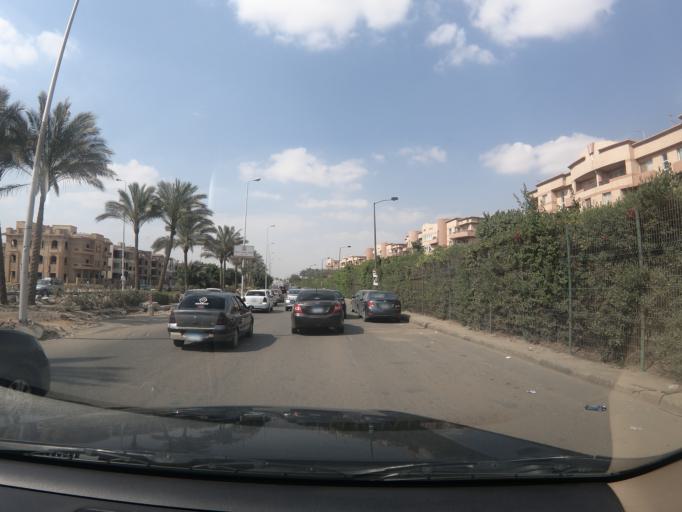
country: EG
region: Muhafazat al Qalyubiyah
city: Al Khankah
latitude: 30.0663
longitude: 31.4752
